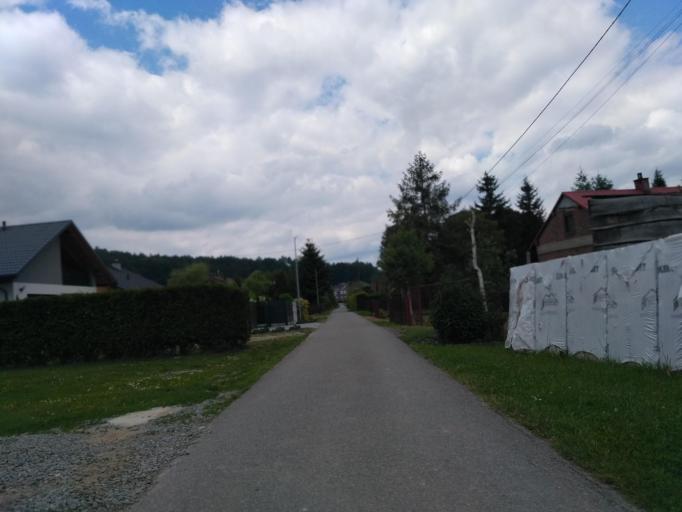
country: PL
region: Subcarpathian Voivodeship
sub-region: Powiat strzyzowski
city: Czudec
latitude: 49.9318
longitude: 21.8514
